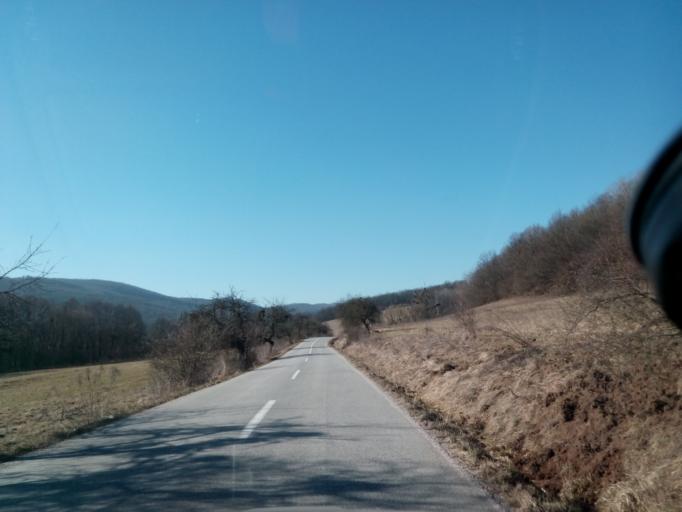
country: SK
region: Kosicky
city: Roznava
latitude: 48.5671
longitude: 20.6350
